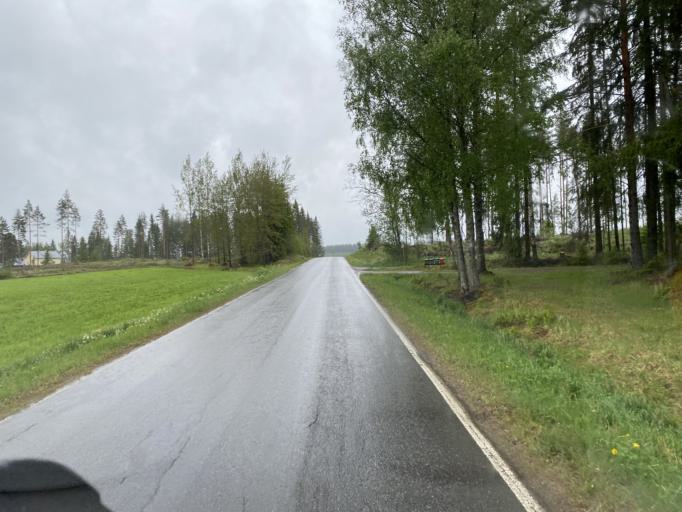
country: FI
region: Haeme
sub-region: Forssa
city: Humppila
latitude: 61.0586
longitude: 23.3254
